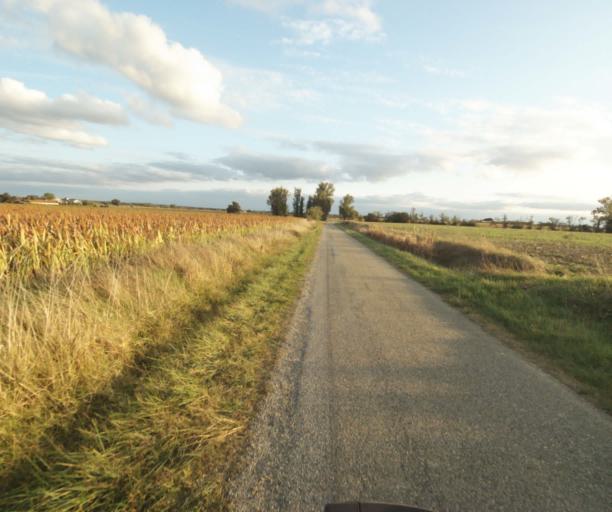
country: FR
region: Midi-Pyrenees
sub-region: Departement de la Haute-Garonne
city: Launac
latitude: 43.8147
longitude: 1.1628
